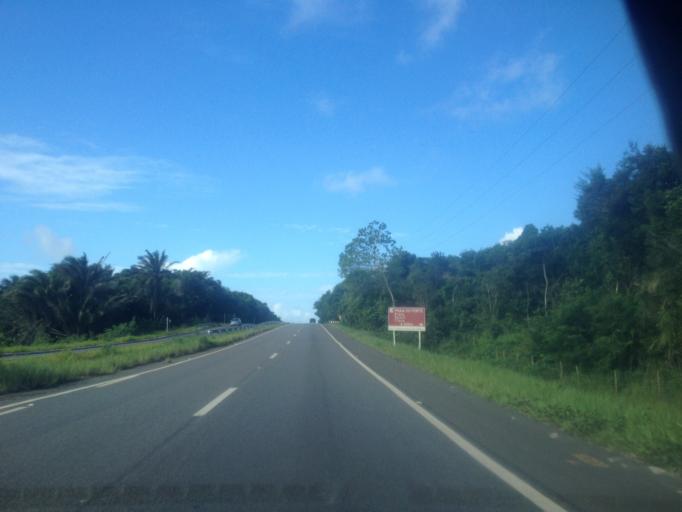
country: BR
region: Bahia
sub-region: Mata De Sao Joao
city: Mata de Sao Joao
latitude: -12.5659
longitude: -38.0248
